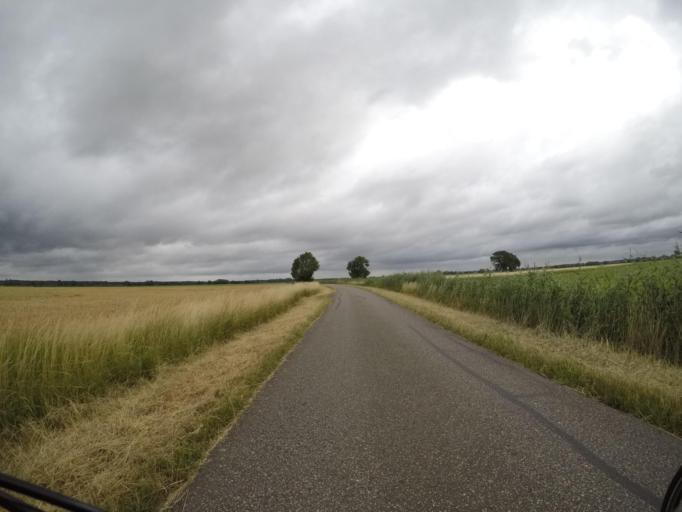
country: DE
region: Lower Saxony
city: Hitzacker
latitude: 53.1646
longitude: 11.0800
